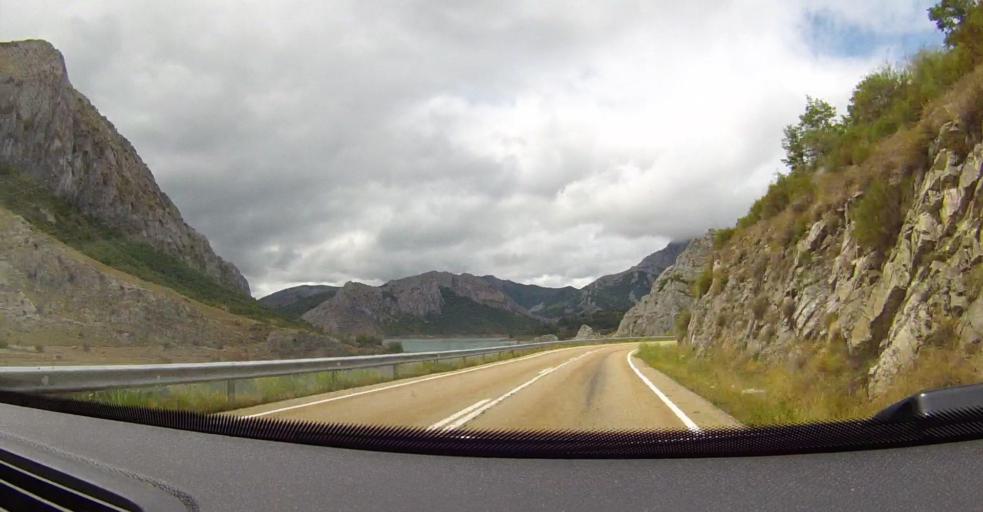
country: ES
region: Castille and Leon
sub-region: Provincia de Leon
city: Reyero
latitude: 42.9577
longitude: -5.2509
